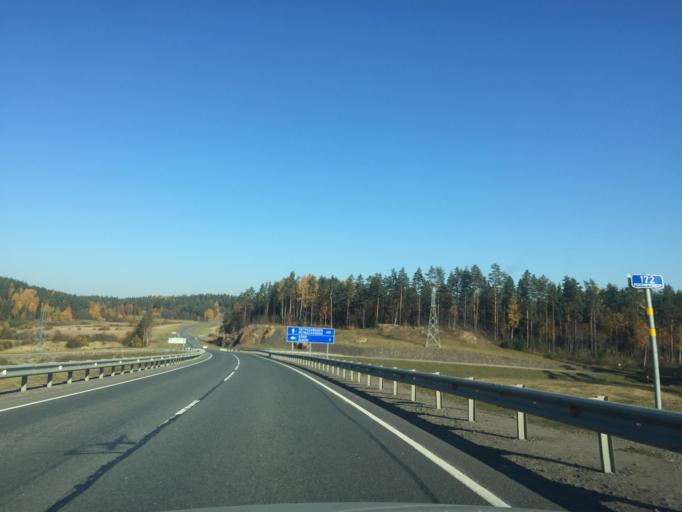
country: RU
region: Leningrad
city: Kuznechnoye
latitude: 61.3005
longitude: 29.7852
